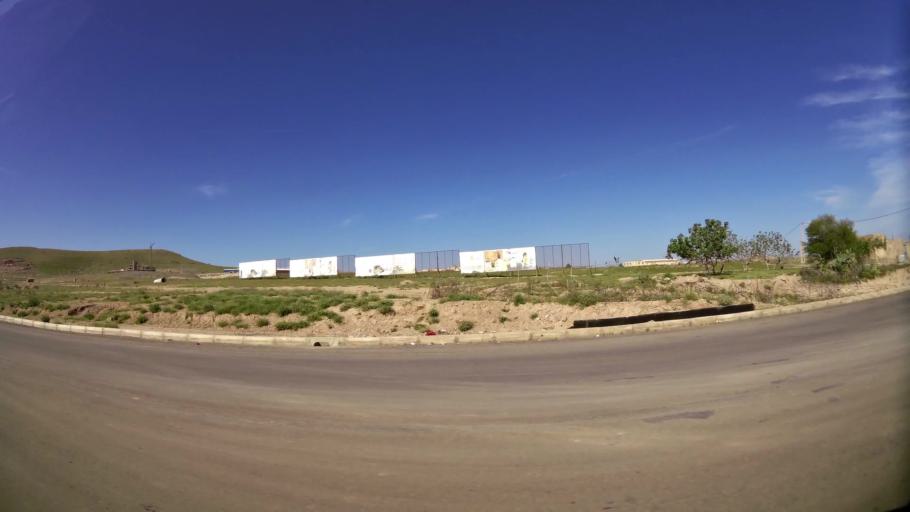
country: MA
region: Oriental
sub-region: Oujda-Angad
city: Oujda
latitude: 34.6538
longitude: -1.9559
